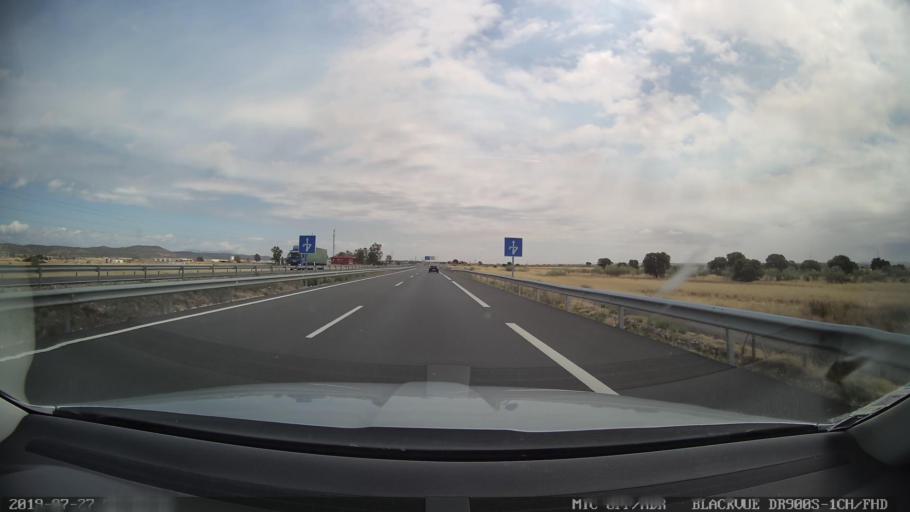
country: ES
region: Castille-La Mancha
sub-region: Province of Toledo
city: Velada
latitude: 39.9402
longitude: -4.9604
